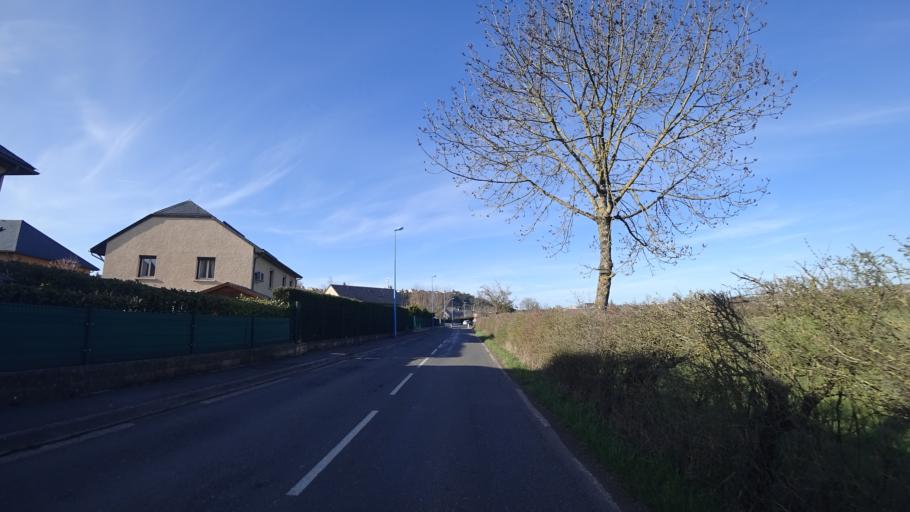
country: FR
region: Midi-Pyrenees
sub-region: Departement de l'Aveyron
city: Rodez
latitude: 44.3692
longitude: 2.5755
